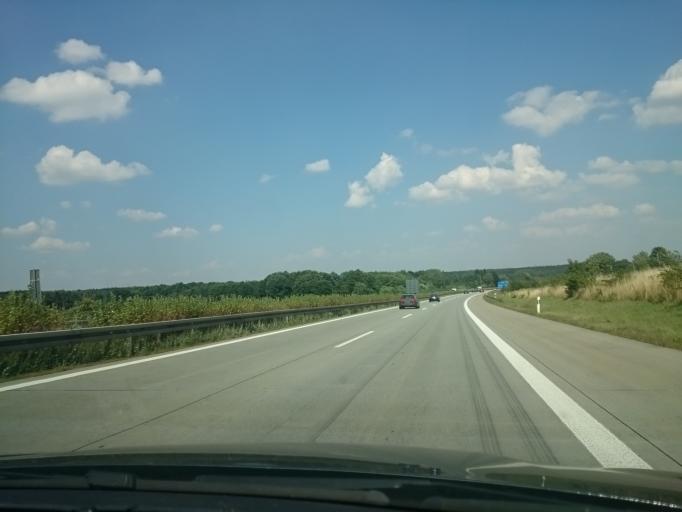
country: DE
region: Saxony
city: Niederdorf
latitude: 50.7333
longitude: 12.7803
